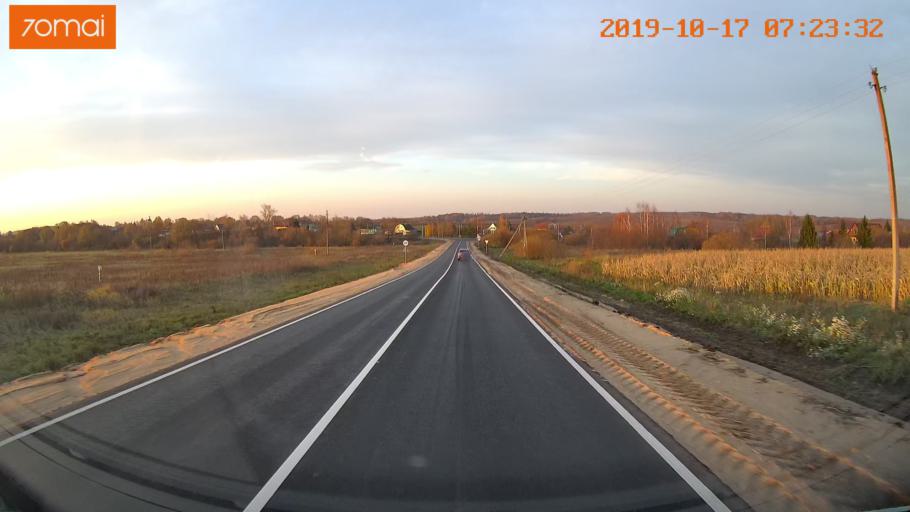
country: RU
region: Ivanovo
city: Gavrilov Posad
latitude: 56.3337
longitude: 40.1200
